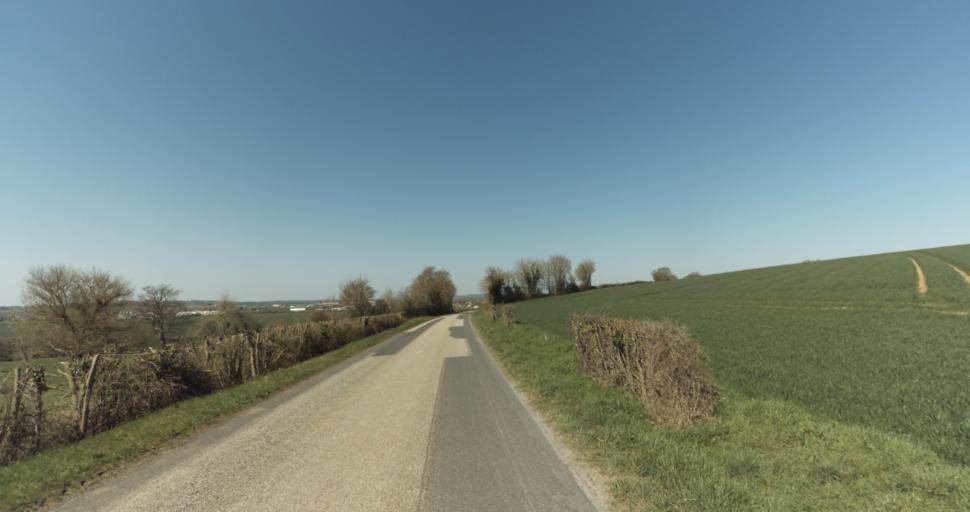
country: FR
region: Lower Normandy
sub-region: Departement du Calvados
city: Saint-Pierre-sur-Dives
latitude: 49.0092
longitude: -0.0173
